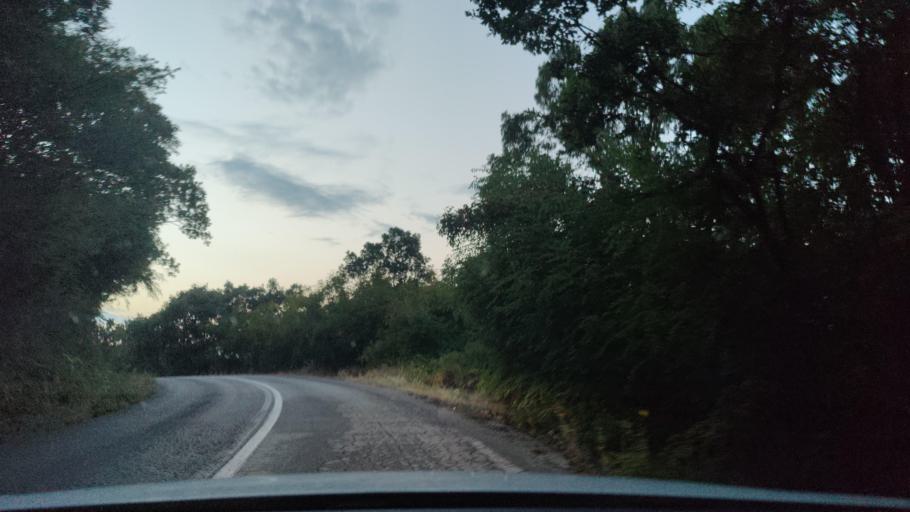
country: GR
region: Central Macedonia
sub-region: Nomos Serron
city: Chrysochorafa
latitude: 41.1805
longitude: 23.1596
